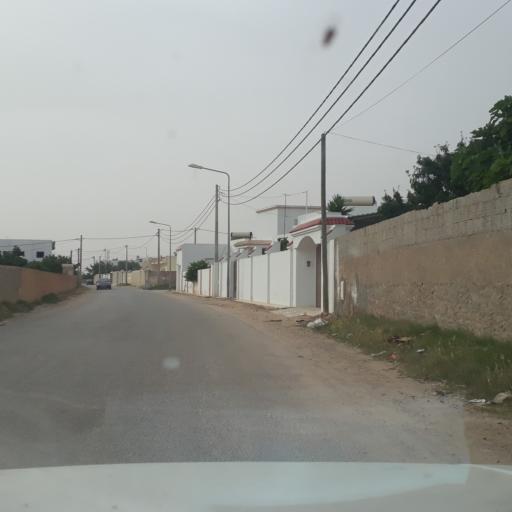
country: TN
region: Safaqis
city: Al Qarmadah
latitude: 34.8194
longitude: 10.7742
